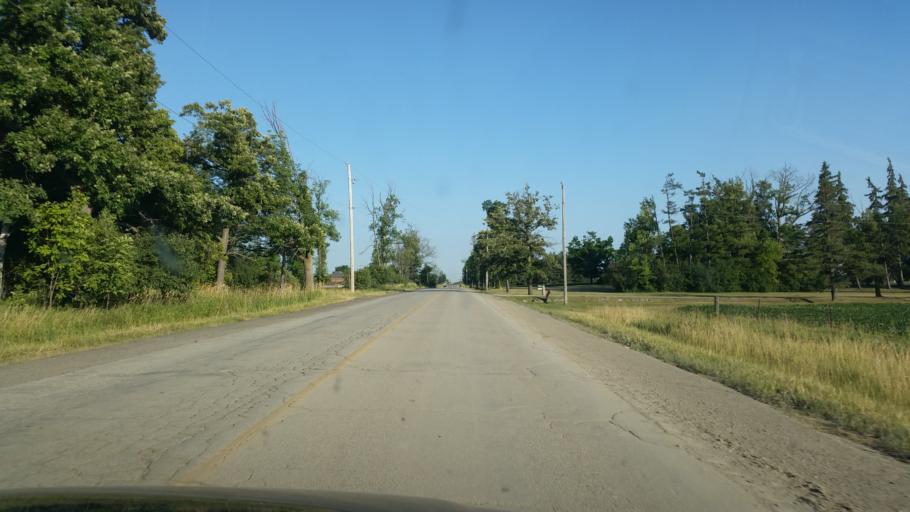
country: CA
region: Ontario
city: Brampton
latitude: 43.7593
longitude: -79.8126
